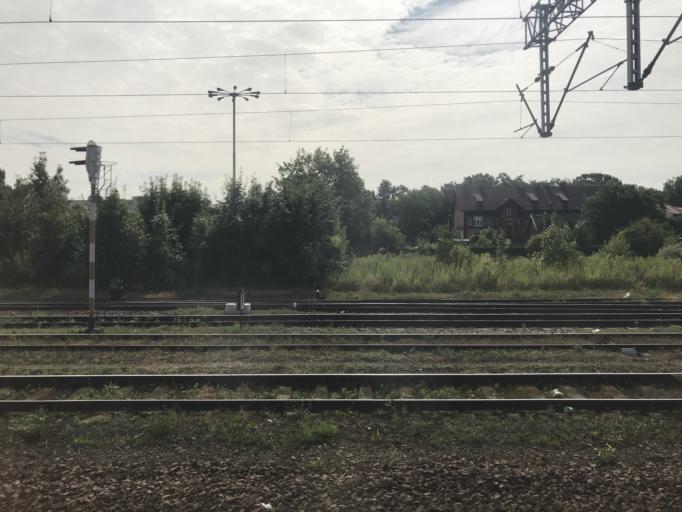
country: PL
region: Kujawsko-Pomorskie
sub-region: Powiat inowroclawski
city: Inowroclaw
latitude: 52.7988
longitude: 18.2373
